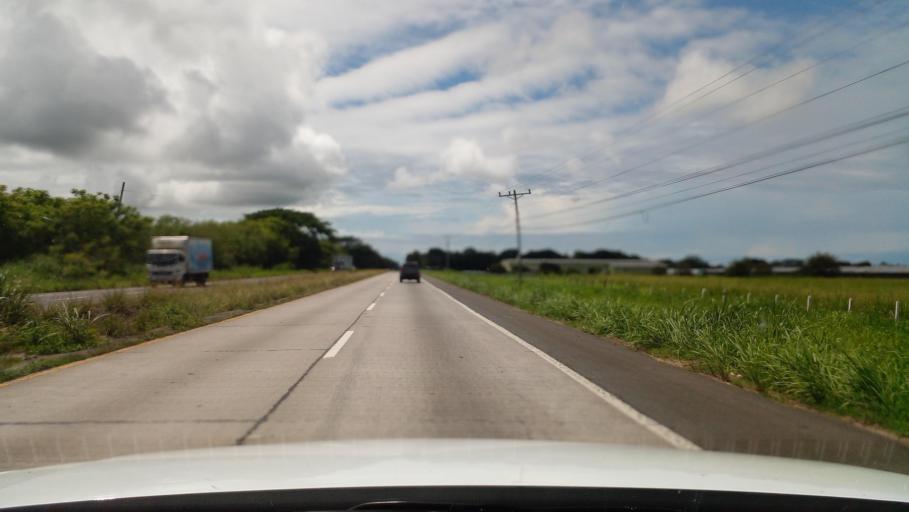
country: PA
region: Cocle
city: Rio Hato
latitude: 8.3851
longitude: -80.1920
